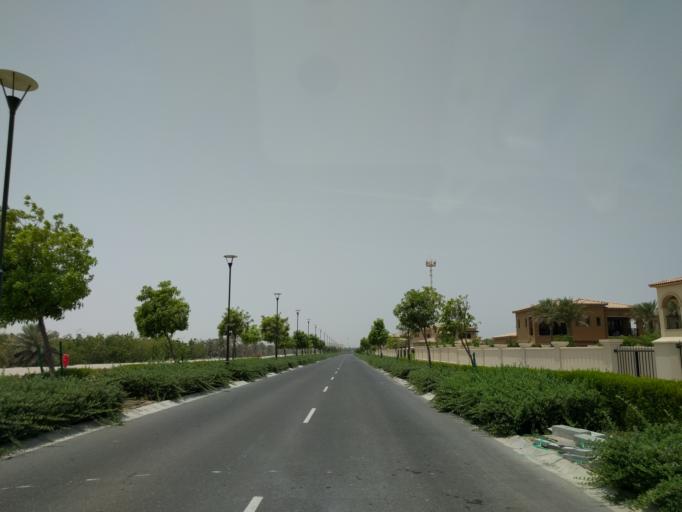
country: AE
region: Abu Dhabi
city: Abu Dhabi
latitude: 24.5474
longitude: 54.4494
